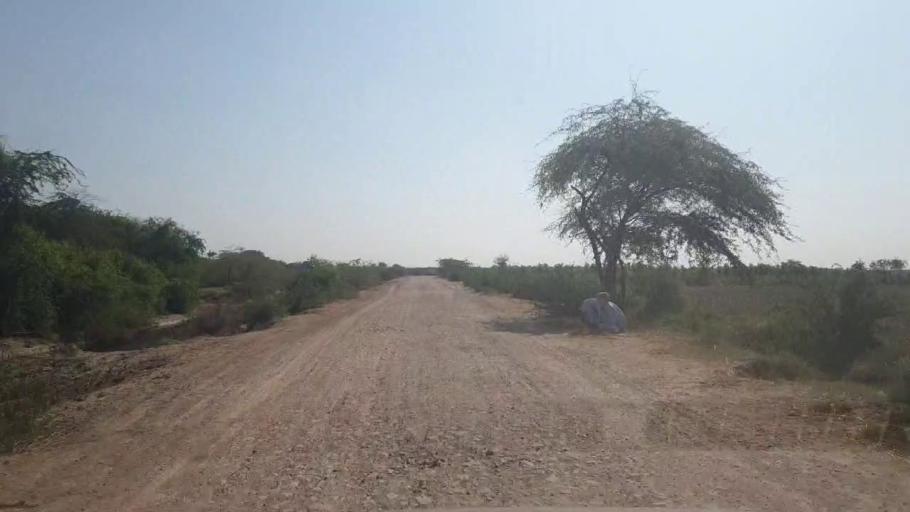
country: PK
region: Sindh
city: Badin
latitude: 24.5975
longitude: 68.8540
